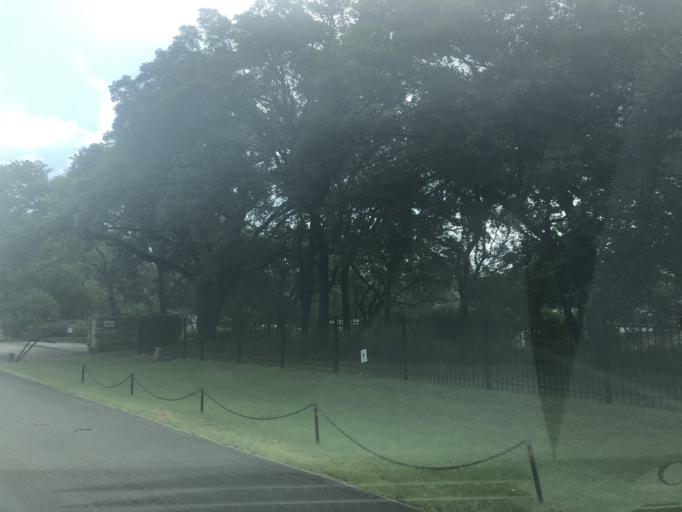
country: US
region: Texas
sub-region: Dallas County
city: University Park
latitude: 32.8675
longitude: -96.8305
